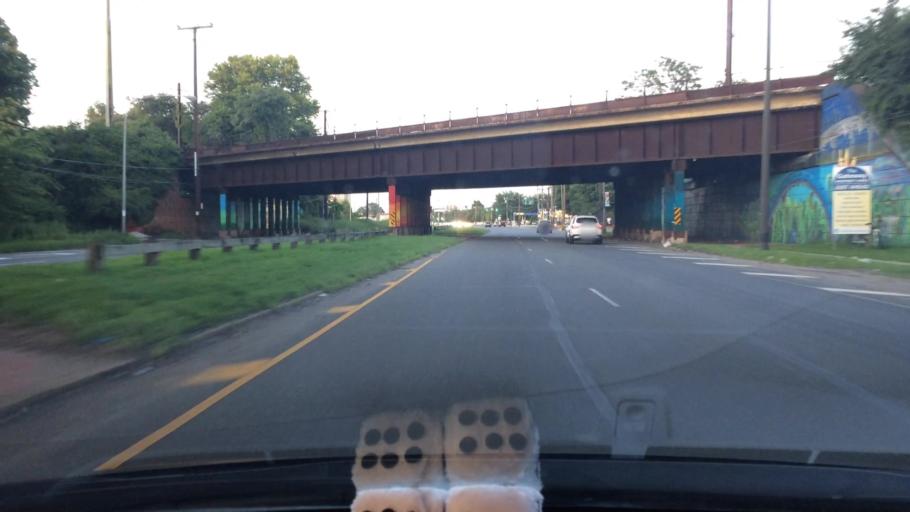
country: US
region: New Jersey
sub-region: Gloucester County
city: National Park
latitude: 39.9062
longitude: -75.1930
